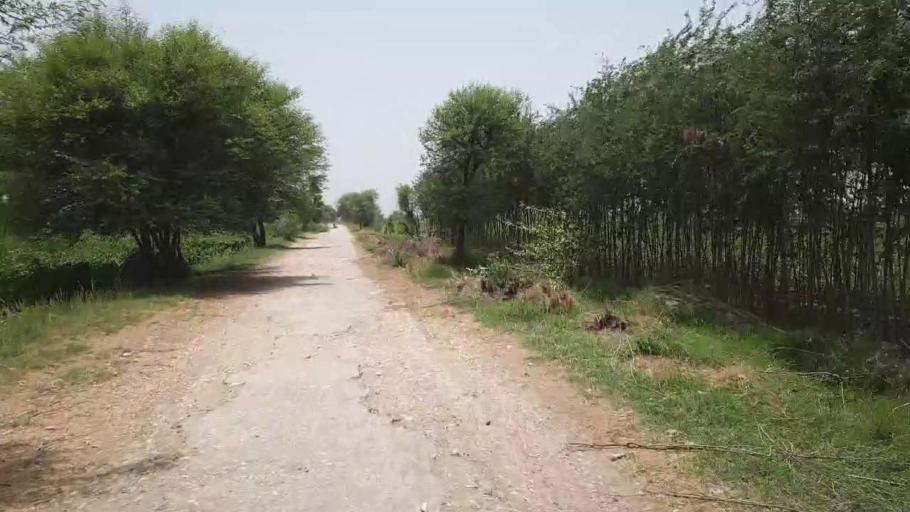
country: PK
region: Sindh
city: Tando Mittha Khan
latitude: 26.0659
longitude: 69.2117
